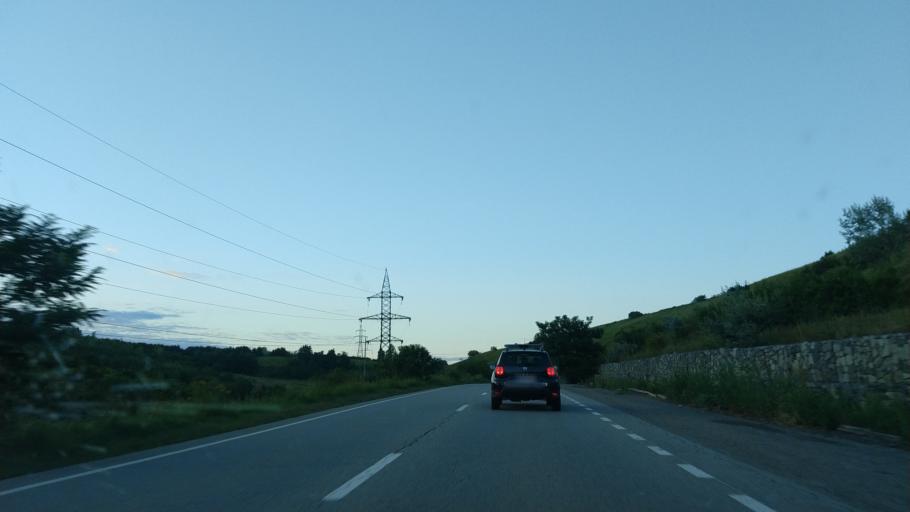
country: RO
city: Vanatori
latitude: 47.2674
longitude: 27.5471
